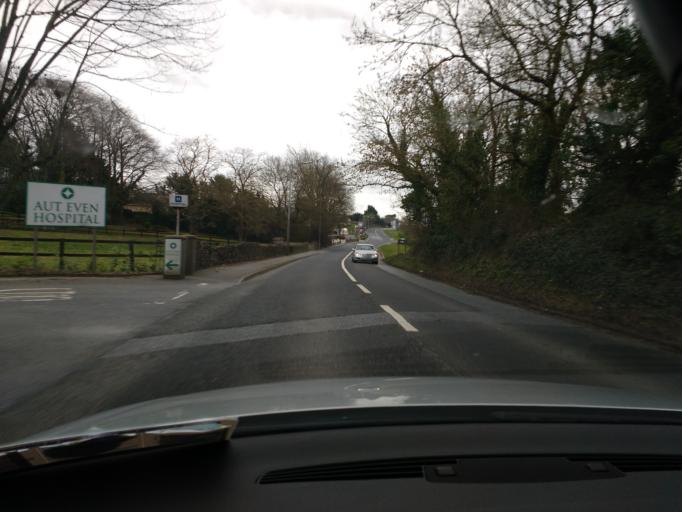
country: IE
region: Leinster
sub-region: Kilkenny
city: Kilkenny
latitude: 52.6754
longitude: -7.2723
